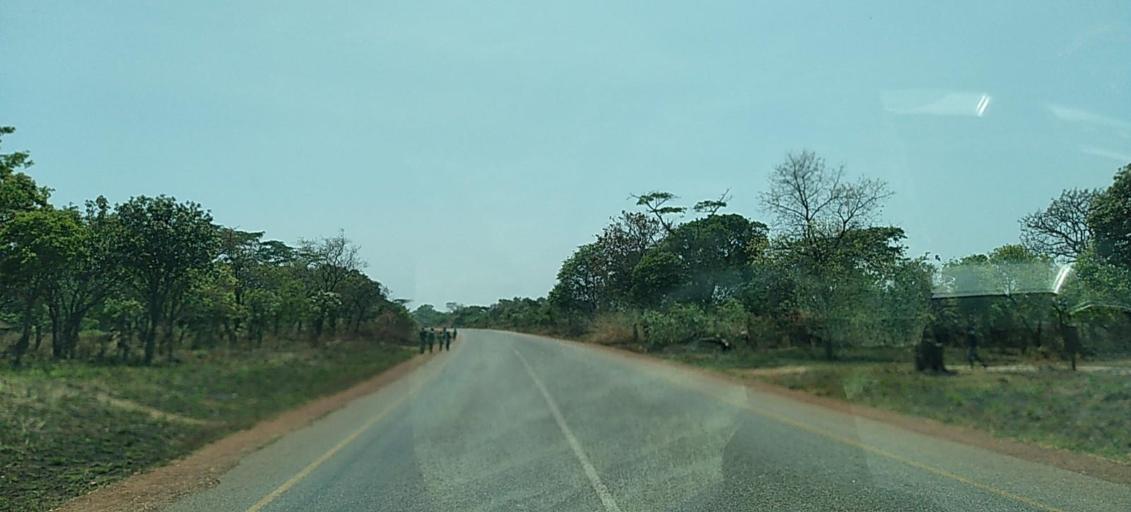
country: ZM
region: North-Western
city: Solwezi
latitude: -12.4027
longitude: 26.1456
